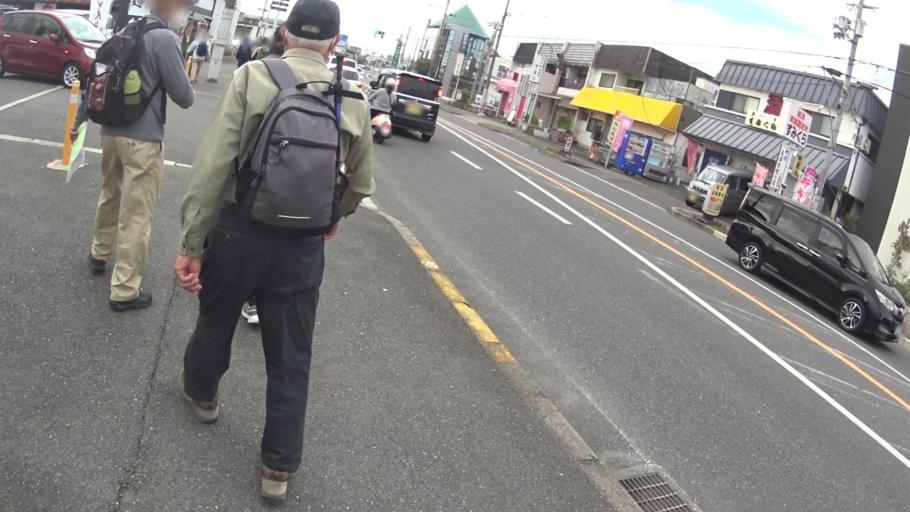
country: JP
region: Osaka
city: Kashihara
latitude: 34.5589
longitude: 135.5943
